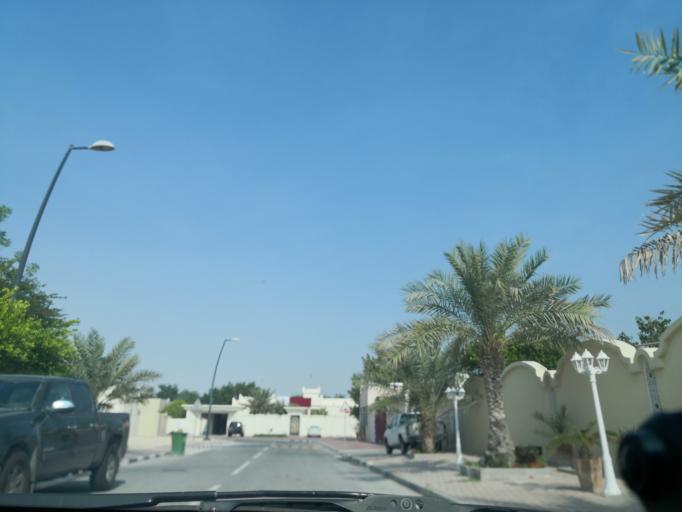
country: QA
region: Baladiyat ad Dawhah
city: Doha
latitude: 25.3471
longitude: 51.4946
